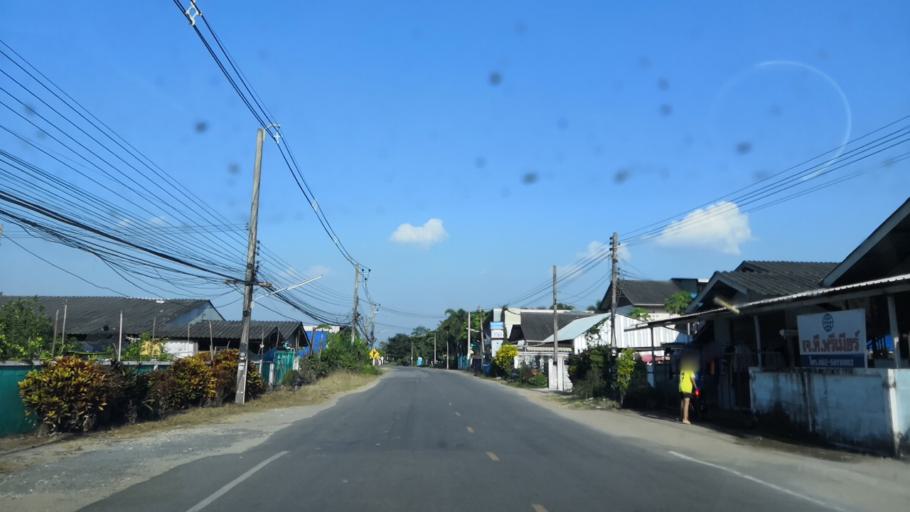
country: TH
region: Chiang Rai
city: Wiang Chai
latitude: 19.9407
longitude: 99.9137
